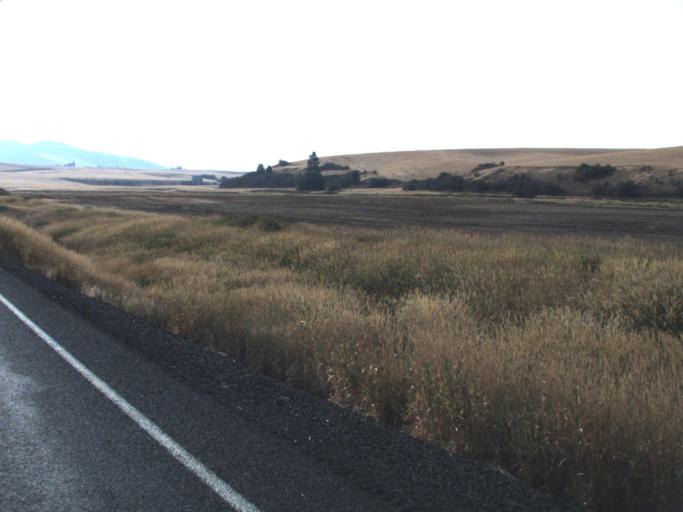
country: US
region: Idaho
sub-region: Benewah County
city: Plummer
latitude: 47.3239
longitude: -117.1833
